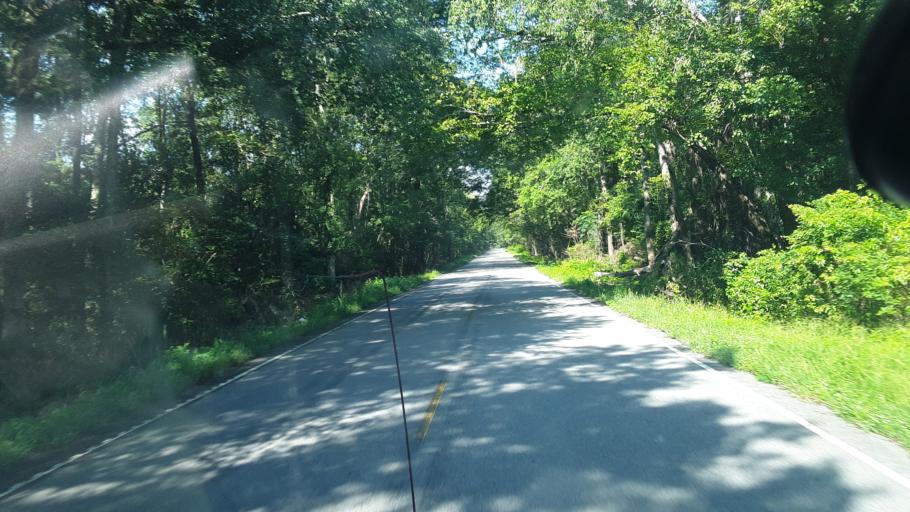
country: US
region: South Carolina
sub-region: Jasper County
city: Ridgeland
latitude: 32.5897
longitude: -80.9543
